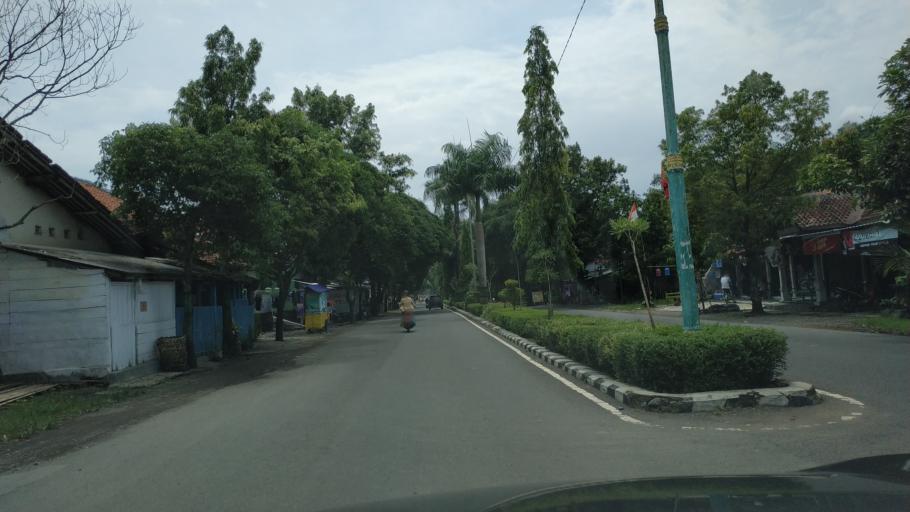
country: ID
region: Central Java
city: Slawi
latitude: -6.9864
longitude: 109.1270
